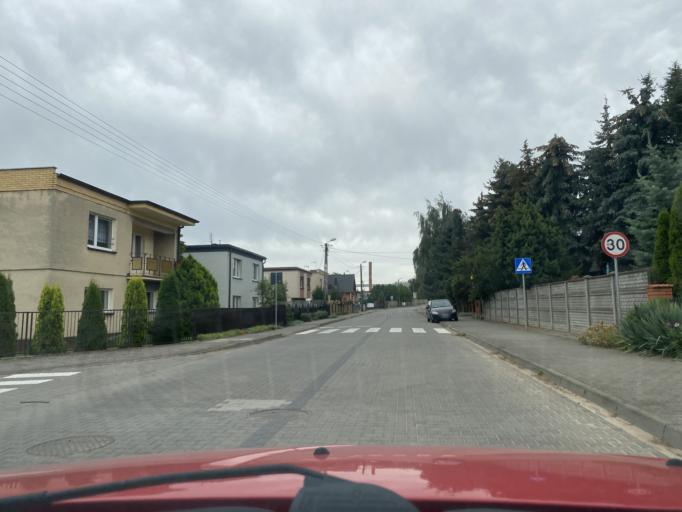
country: PL
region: Greater Poland Voivodeship
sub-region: Powiat poznanski
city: Tarnowo Podgorne
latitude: 52.4612
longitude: 16.6563
